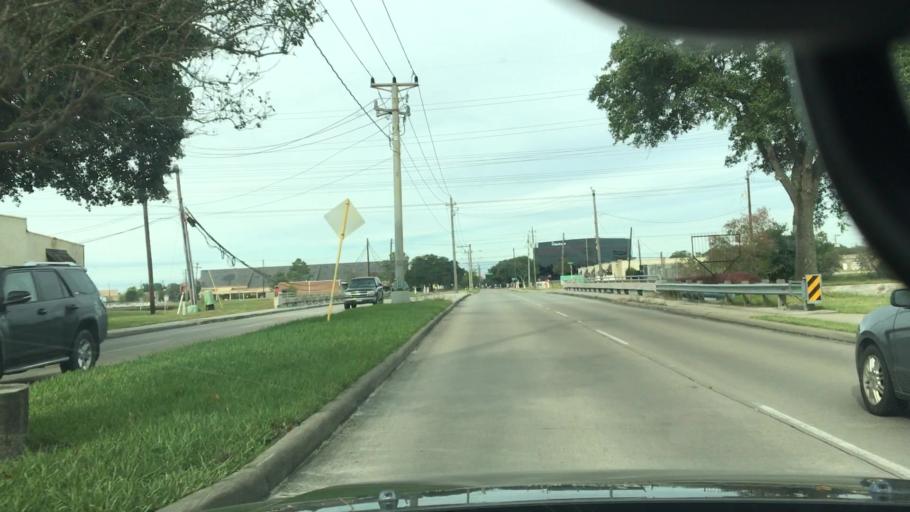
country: US
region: Texas
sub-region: Harris County
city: Webster
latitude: 29.5502
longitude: -95.1111
